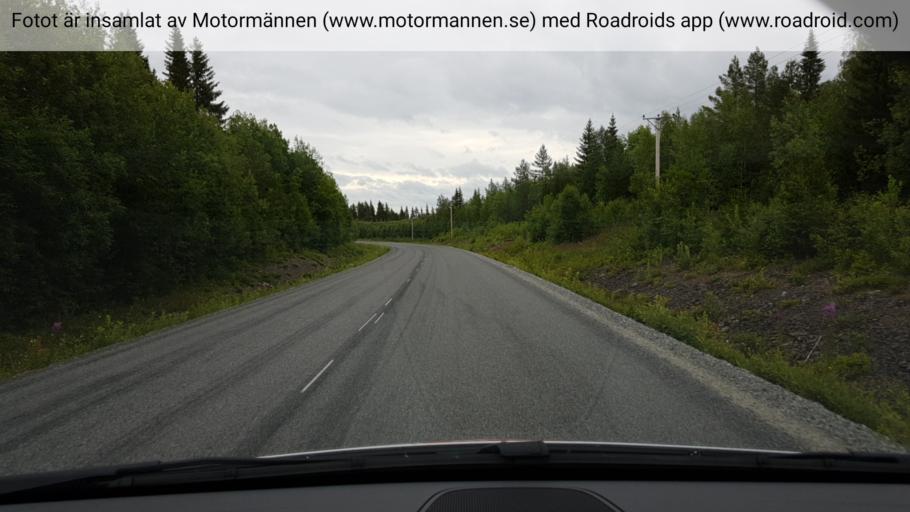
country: SE
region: Jaemtland
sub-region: Krokoms Kommun
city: Krokom
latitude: 63.6624
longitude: 14.4996
